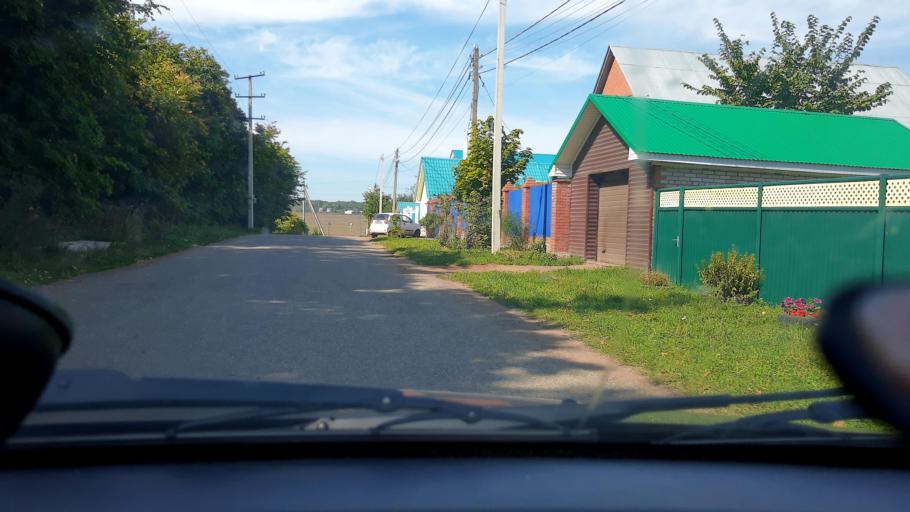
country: RU
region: Bashkortostan
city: Avdon
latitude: 54.6752
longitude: 55.7083
